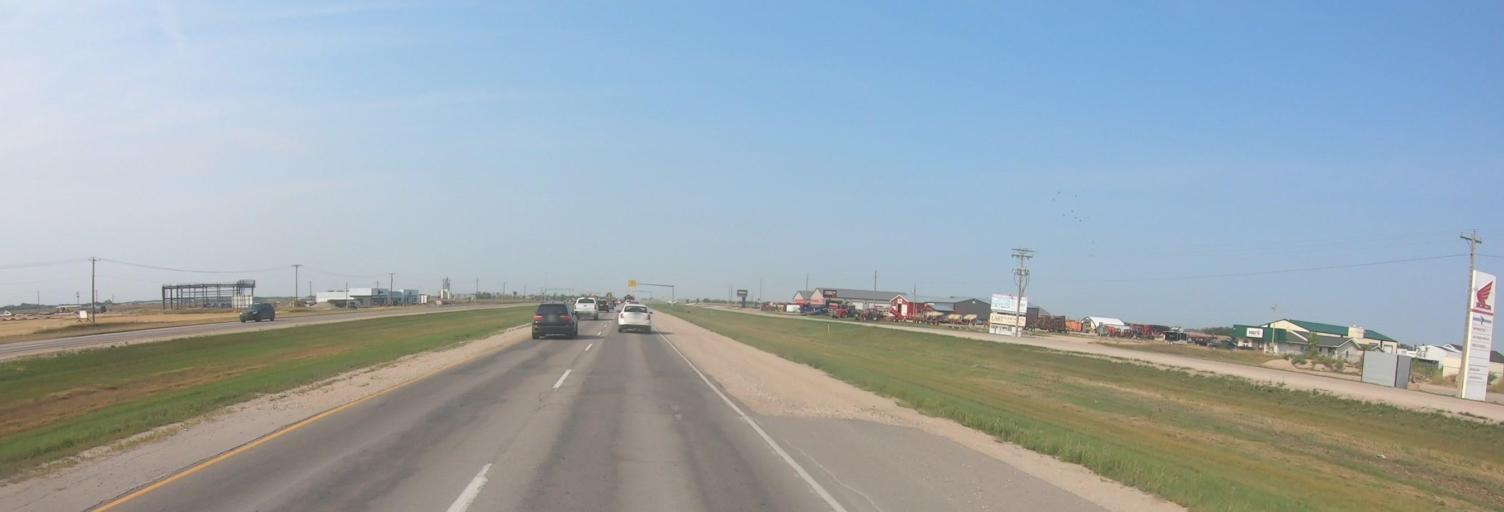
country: CA
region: Manitoba
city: Steinbach
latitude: 49.5635
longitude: -96.6878
